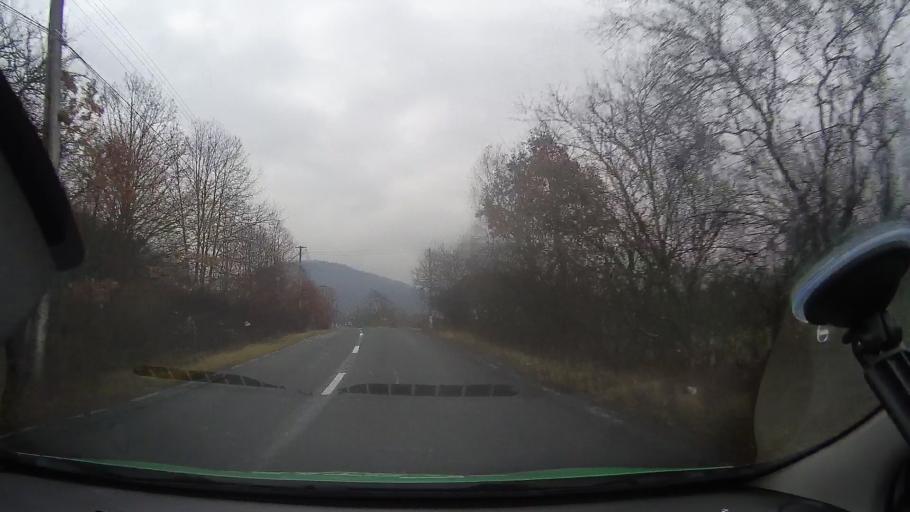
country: RO
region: Arad
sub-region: Comuna Plescuta
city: Plescuta
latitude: 46.2959
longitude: 22.4327
